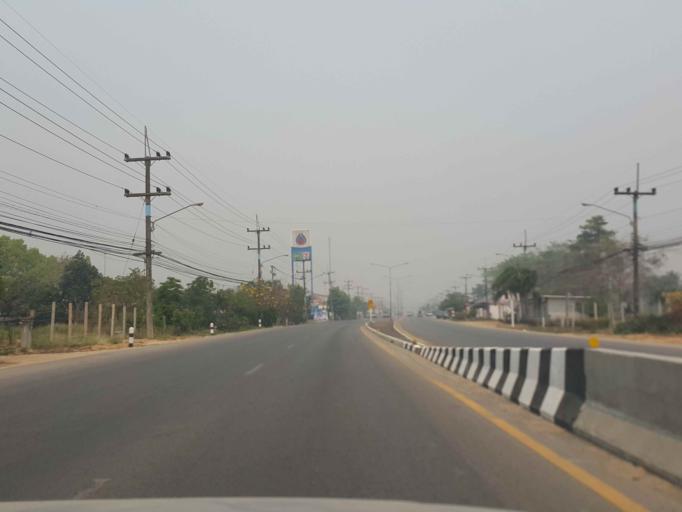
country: TH
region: Chiang Mai
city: Mae Taeng
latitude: 19.0809
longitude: 98.9372
